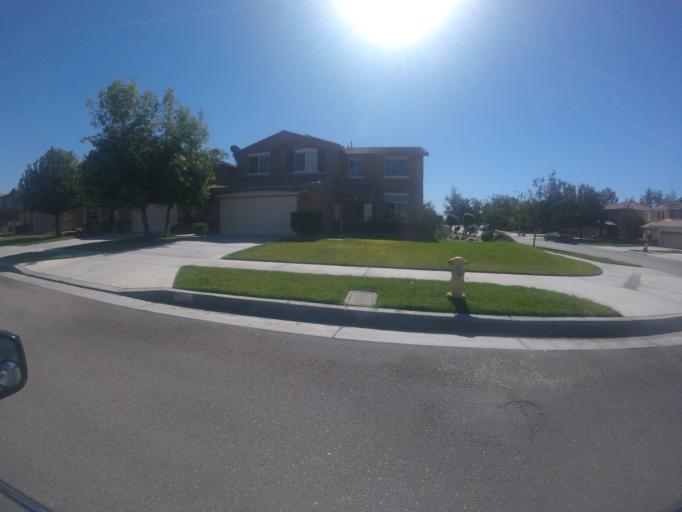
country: US
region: California
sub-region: San Bernardino County
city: Redlands
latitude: 34.0824
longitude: -117.1674
